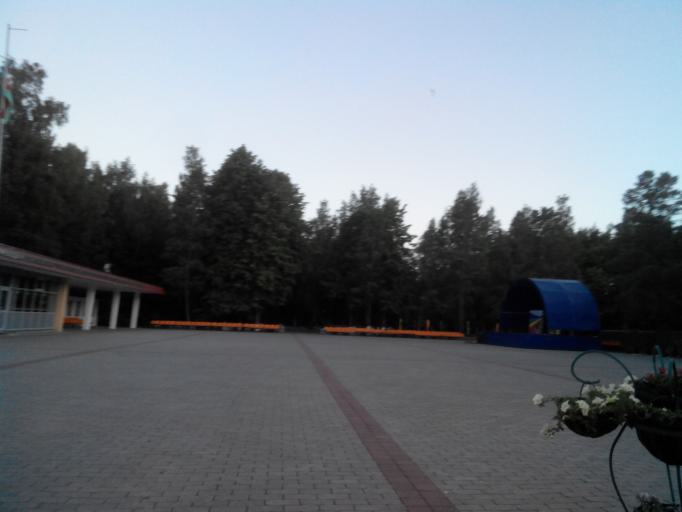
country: BY
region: Minsk
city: Narach
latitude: 54.8330
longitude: 26.7126
